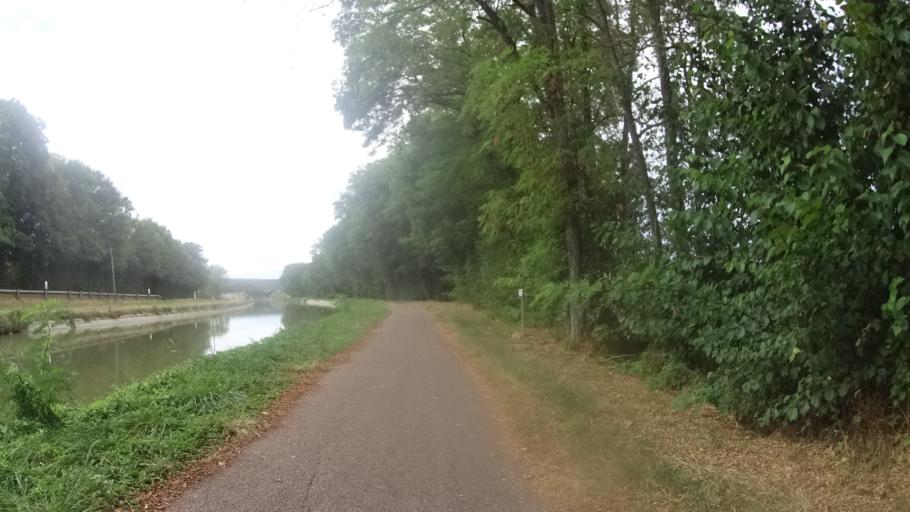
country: FR
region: Bourgogne
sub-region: Departement de la Nievre
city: Imphy
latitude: 46.9318
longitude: 3.2235
